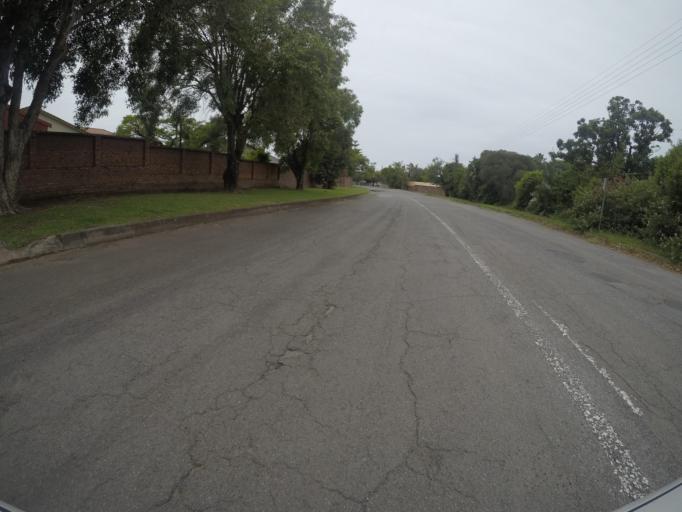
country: ZA
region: Eastern Cape
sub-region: Buffalo City Metropolitan Municipality
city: East London
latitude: -32.9749
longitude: 27.9365
